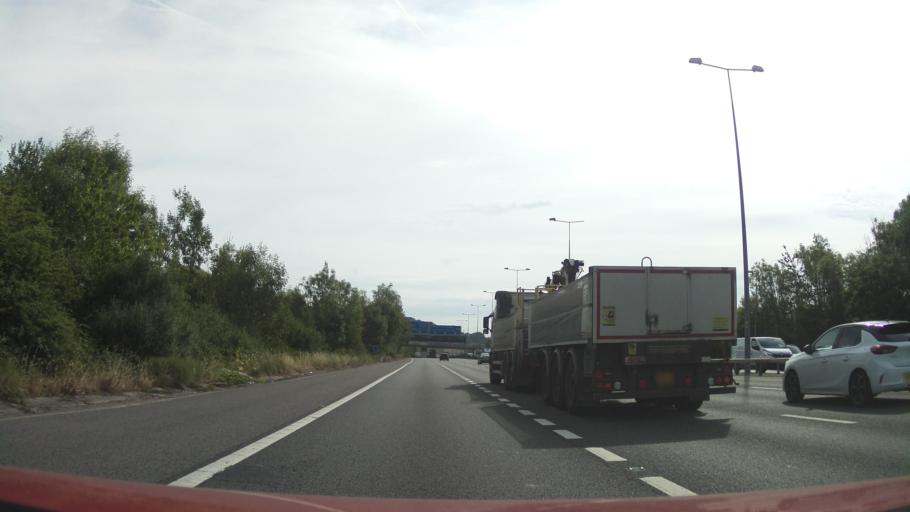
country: GB
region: England
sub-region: Surrey
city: Godstone
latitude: 51.2591
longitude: -0.0751
